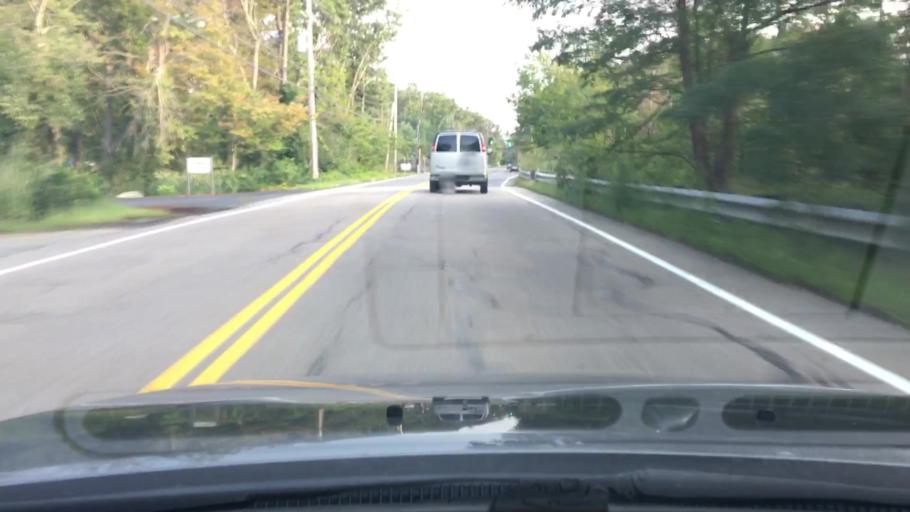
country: US
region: Massachusetts
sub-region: Middlesex County
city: Hopkinton
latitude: 42.1931
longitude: -71.5403
